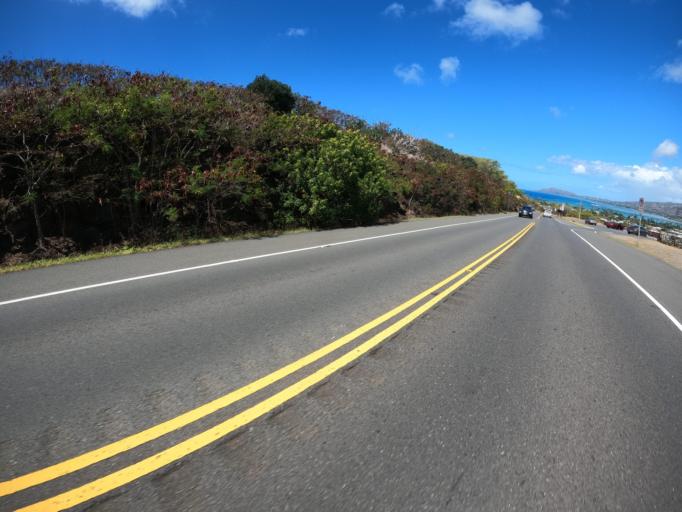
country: US
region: Hawaii
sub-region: Honolulu County
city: Waimanalo Beach
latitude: 21.2760
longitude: -157.6953
